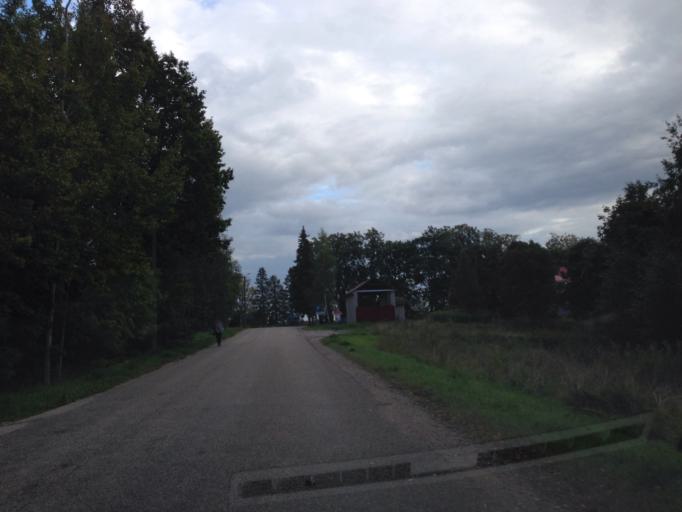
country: EE
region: Tartu
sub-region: Puhja vald
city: Puhja
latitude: 58.1803
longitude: 26.1971
